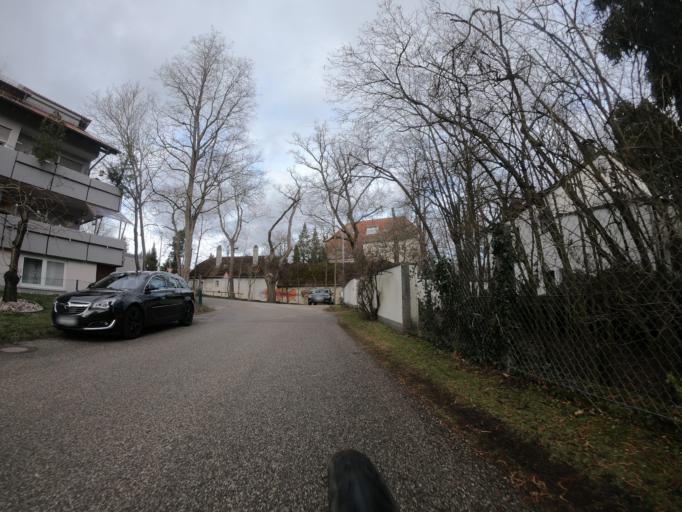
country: DE
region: Bavaria
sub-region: Upper Bavaria
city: Fuerstenfeldbruck
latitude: 48.1808
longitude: 11.2663
